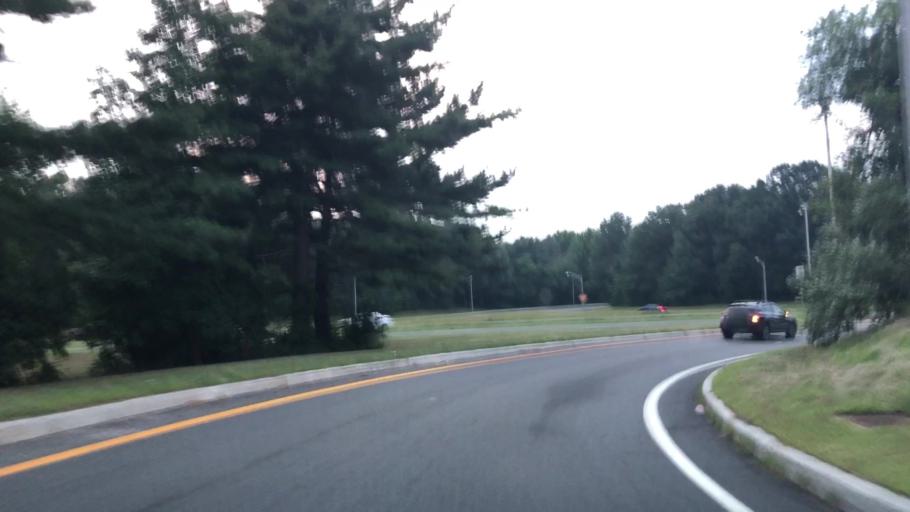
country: US
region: New Jersey
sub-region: Ocean County
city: Vista Center
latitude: 40.1602
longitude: -74.4219
